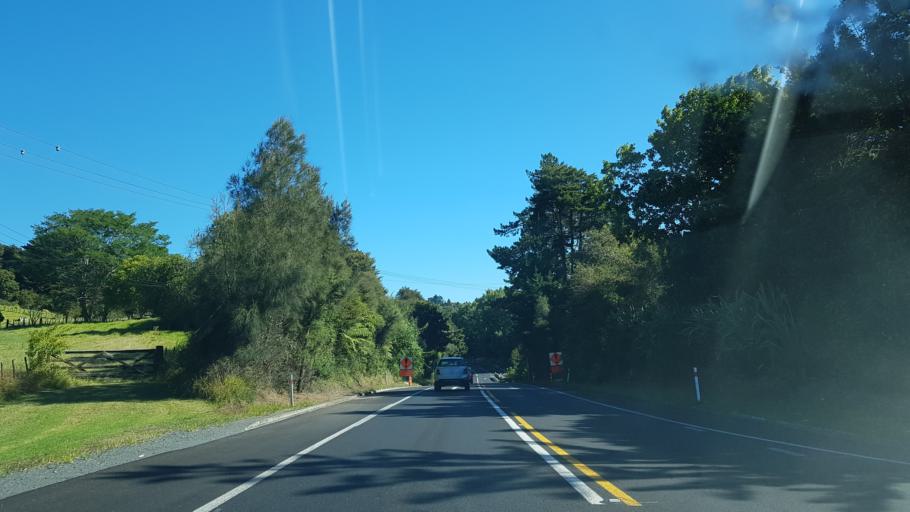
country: NZ
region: Auckland
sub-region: Auckland
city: Warkworth
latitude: -36.4339
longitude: 174.6495
